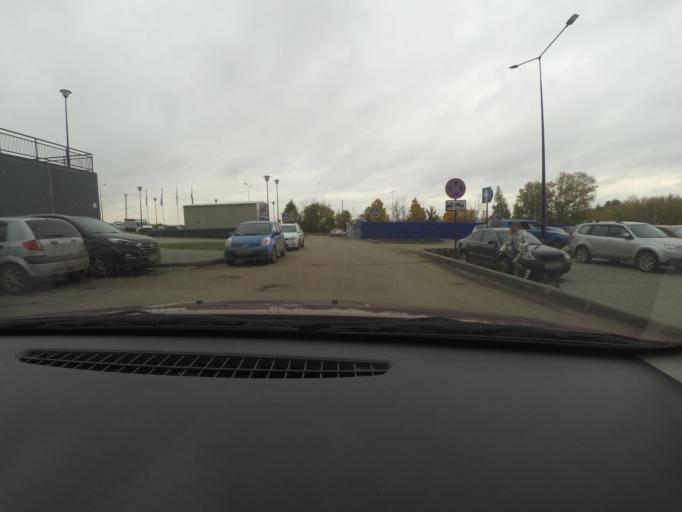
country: RU
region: Nizjnij Novgorod
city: Afonino
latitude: 56.2502
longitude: 44.0429
